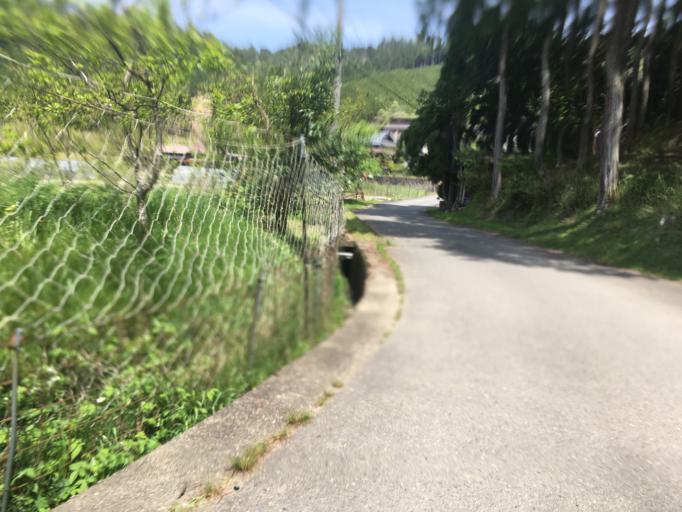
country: JP
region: Kyoto
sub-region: Kyoto-shi
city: Kamigyo-ku
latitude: 35.0837
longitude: 135.7219
